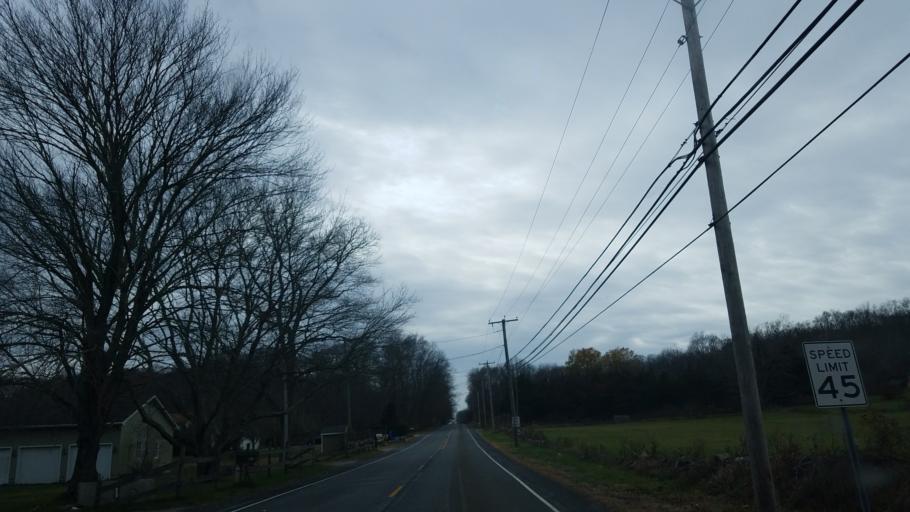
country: US
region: Connecticut
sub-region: New London County
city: Montville Center
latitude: 41.5737
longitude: -72.2123
